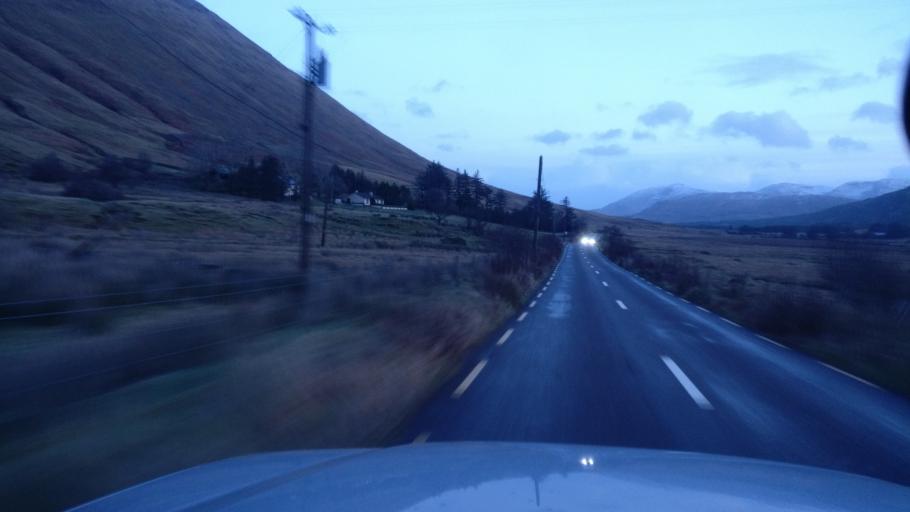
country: IE
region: Connaught
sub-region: Maigh Eo
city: Westport
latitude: 53.5691
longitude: -9.6555
